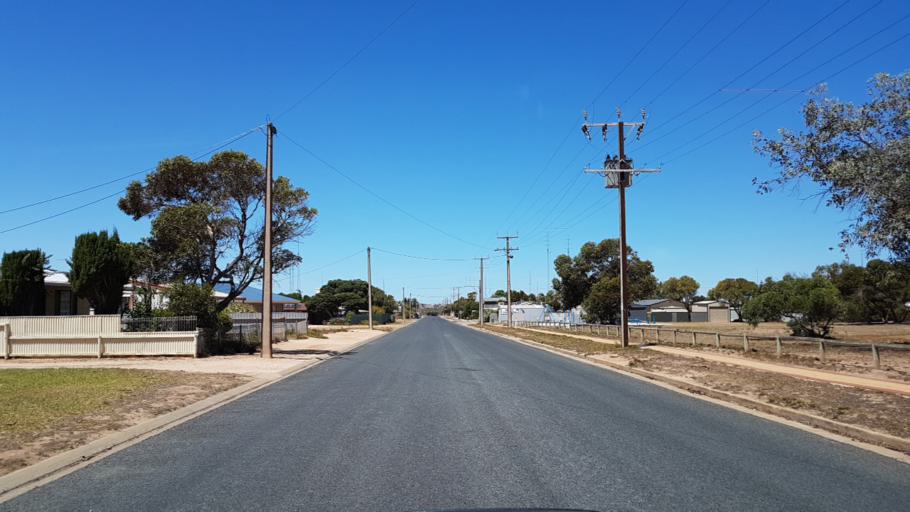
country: AU
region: South Australia
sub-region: Copper Coast
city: Wallaroo
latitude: -33.9004
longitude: 137.6309
